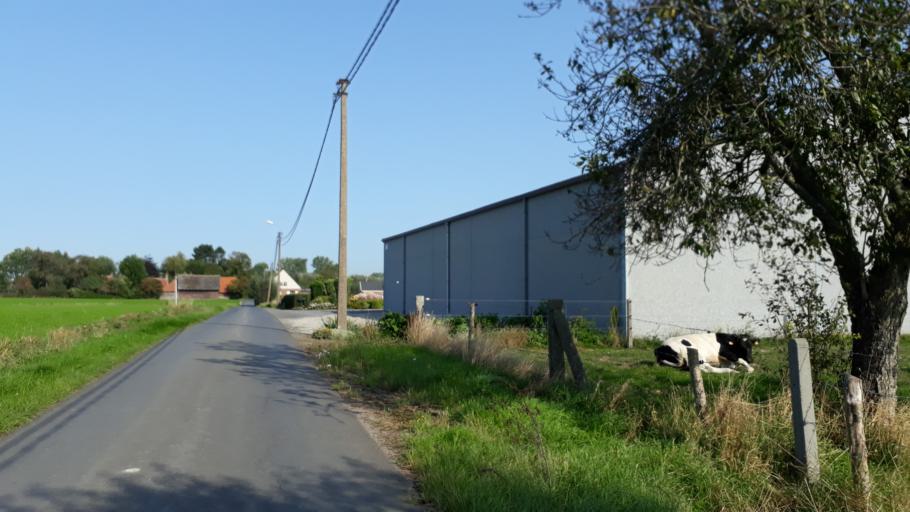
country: BE
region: Flanders
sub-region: Provincie West-Vlaanderen
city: Kortemark
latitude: 51.0240
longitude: 3.0775
